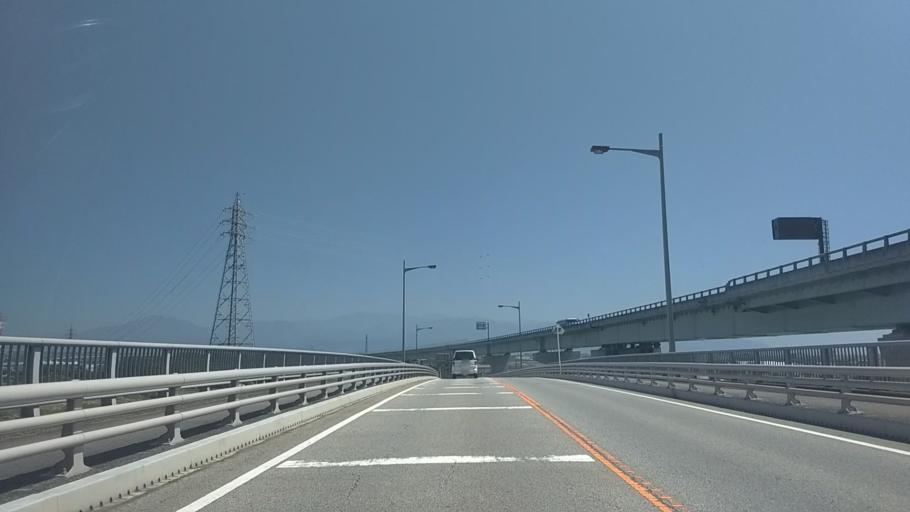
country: JP
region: Yamanashi
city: Ryuo
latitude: 35.5678
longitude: 138.4743
